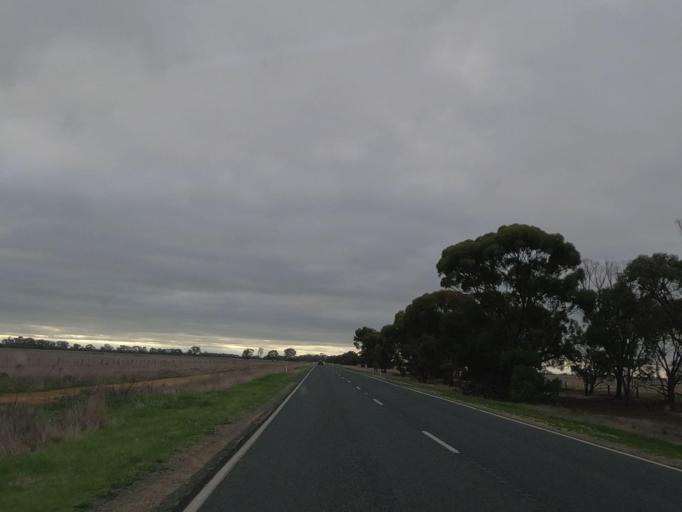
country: AU
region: Victoria
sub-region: Swan Hill
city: Swan Hill
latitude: -35.9639
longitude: 143.9429
